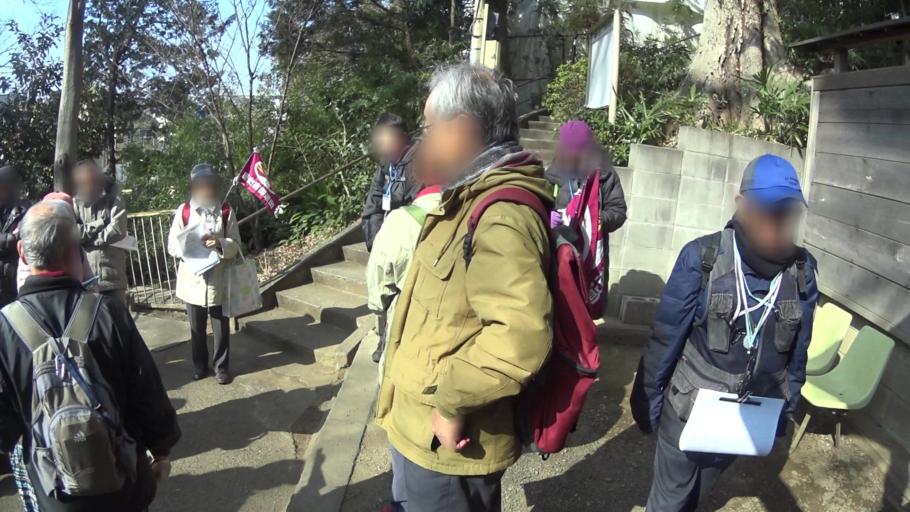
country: JP
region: Tokyo
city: Kokubunji
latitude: 35.6660
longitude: 139.4950
